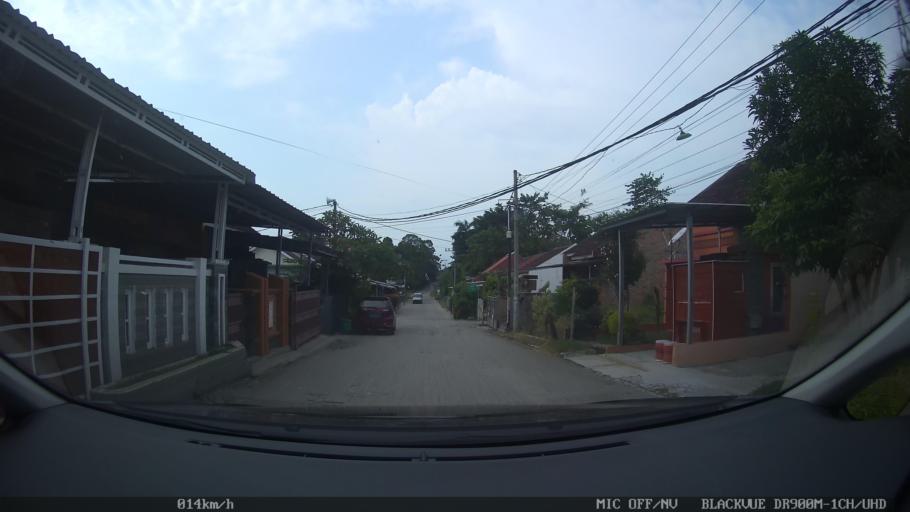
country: ID
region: Lampung
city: Kedaton
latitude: -5.3682
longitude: 105.2161
